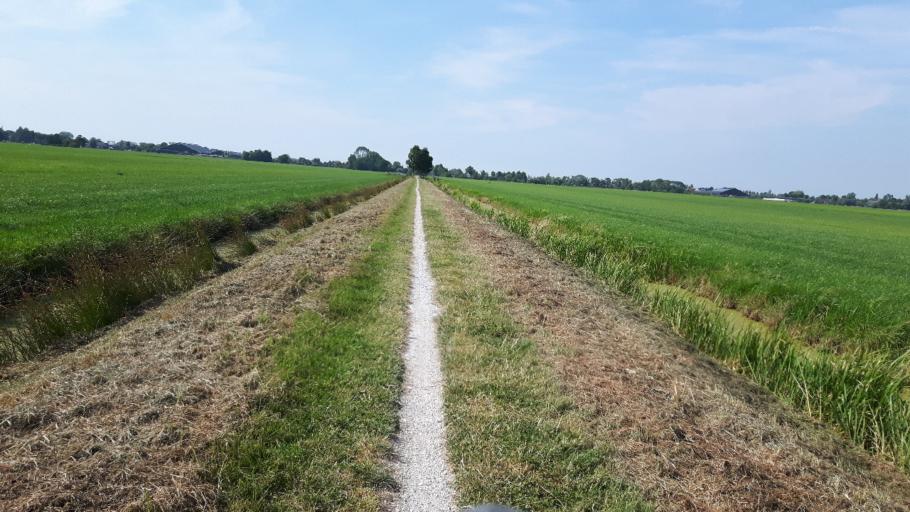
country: NL
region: Utrecht
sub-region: Gemeente Oudewater
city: Oudewater
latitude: 51.9795
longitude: 4.8890
